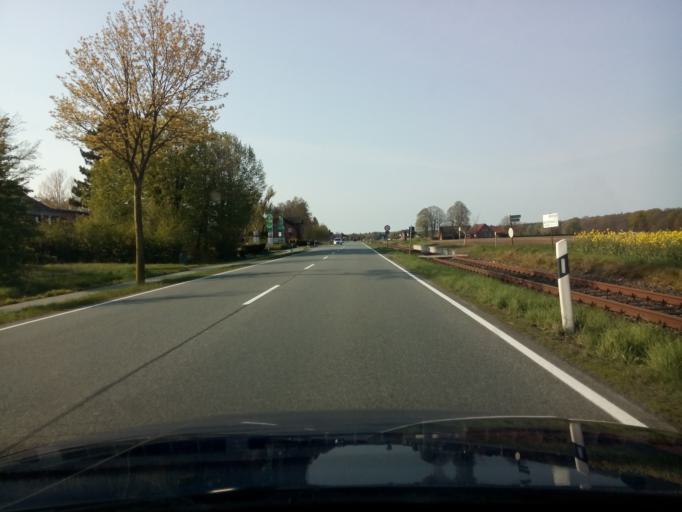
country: DE
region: Lower Saxony
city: Syke
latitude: 52.8959
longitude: 8.8464
